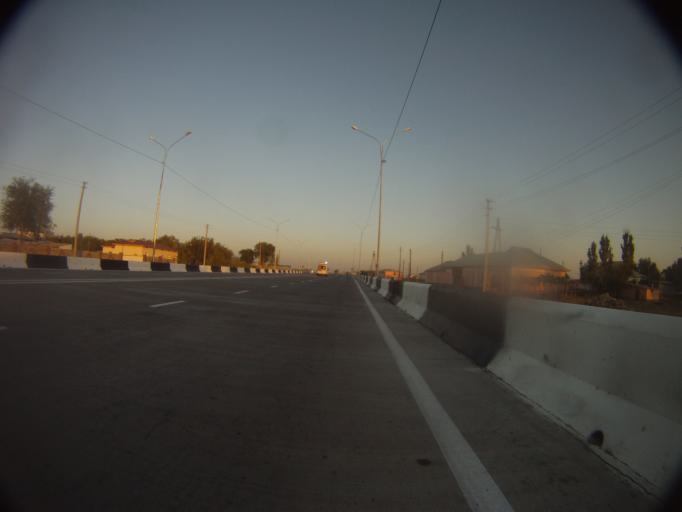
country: KZ
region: Ongtustik Qazaqstan
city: Turkestan
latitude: 43.2564
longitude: 68.3855
